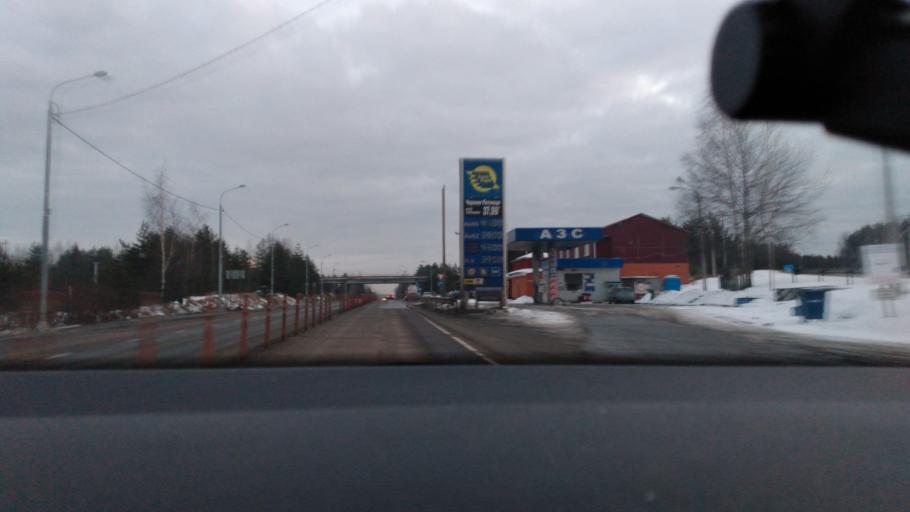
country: RU
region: Moskovskaya
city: Yegor'yevsk
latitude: 55.4174
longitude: 39.0437
